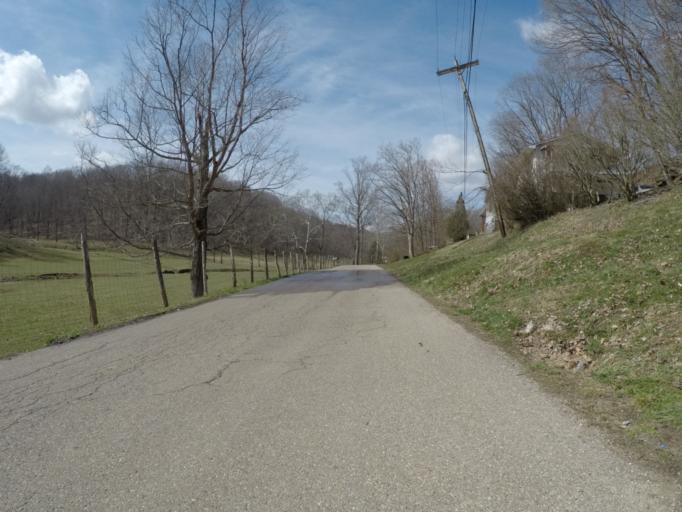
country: US
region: Ohio
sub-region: Lawrence County
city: Burlington
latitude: 38.4780
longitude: -82.5138
